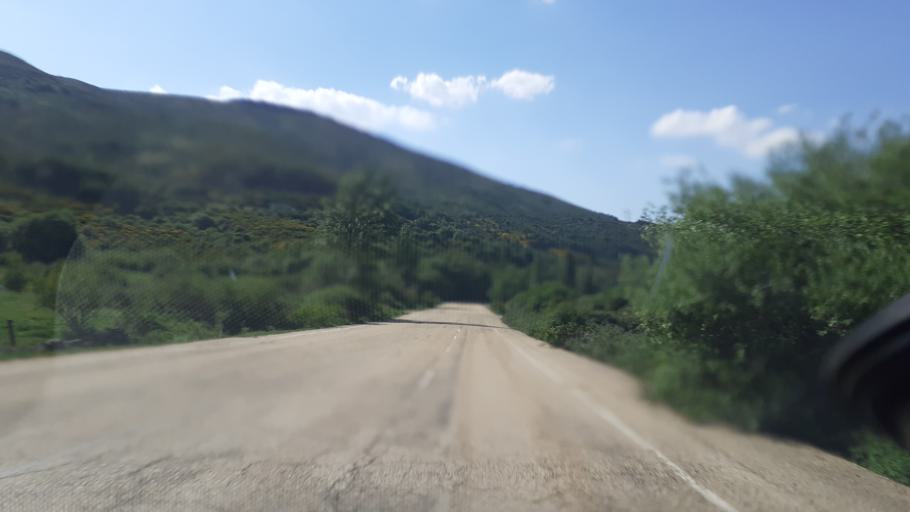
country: ES
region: Madrid
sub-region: Provincia de Madrid
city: Somosierra
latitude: 41.1468
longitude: -3.5796
